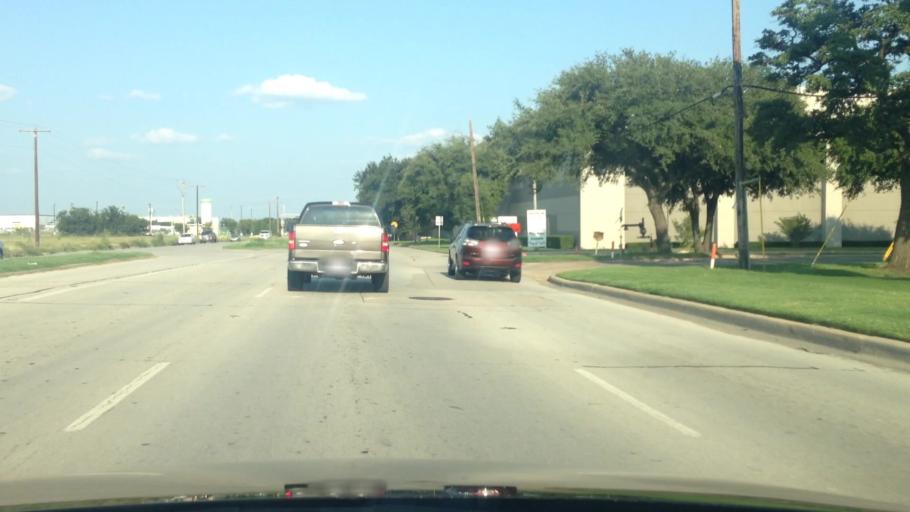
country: US
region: Texas
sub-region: Tarrant County
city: Everman
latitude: 32.6275
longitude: -97.3203
